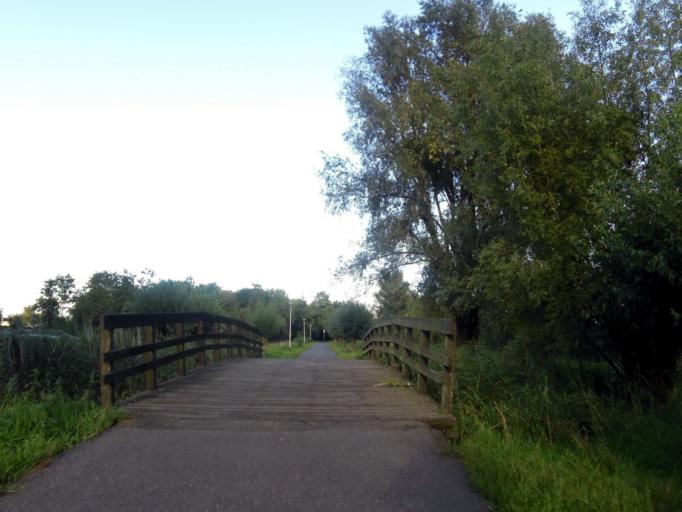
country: NL
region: South Holland
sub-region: Gemeente Alphen aan den Rijn
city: Alphen aan den Rijn
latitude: 52.1227
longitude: 4.6373
